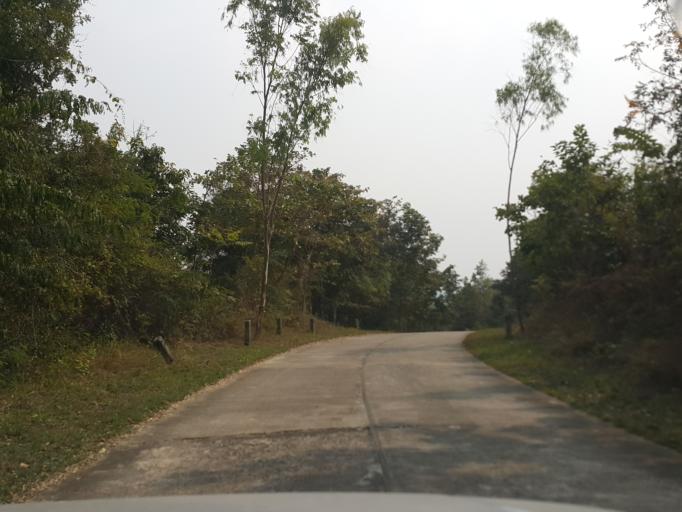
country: TH
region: Lampang
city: Thoen
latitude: 17.6364
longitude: 99.2531
